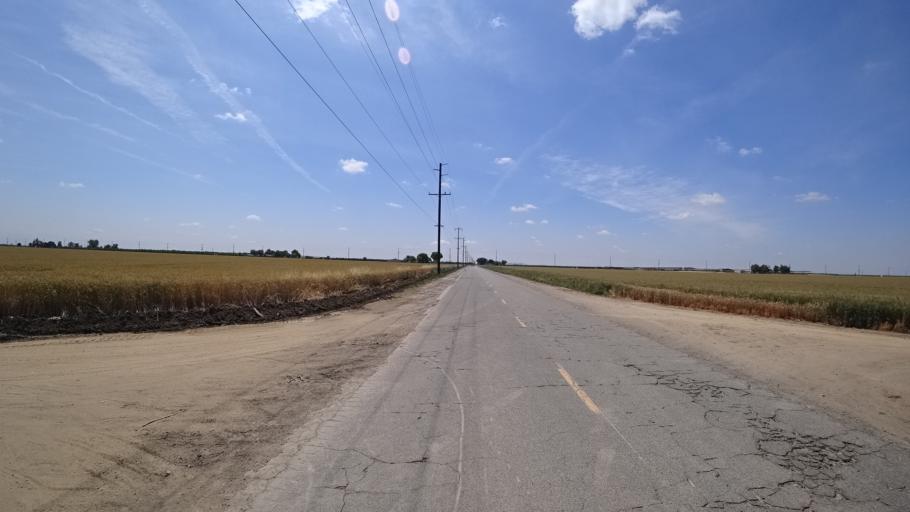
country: US
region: California
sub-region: Tulare County
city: Goshen
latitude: 36.2877
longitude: -119.4744
